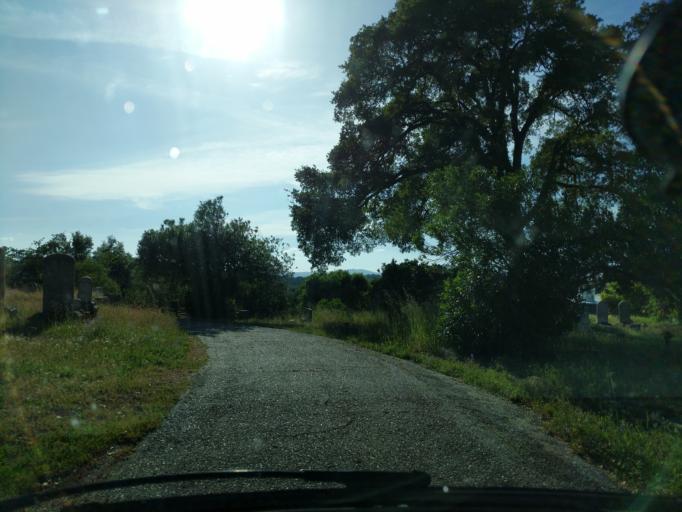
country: US
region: California
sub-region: Calaveras County
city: Angels Camp
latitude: 38.0791
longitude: -120.5589
